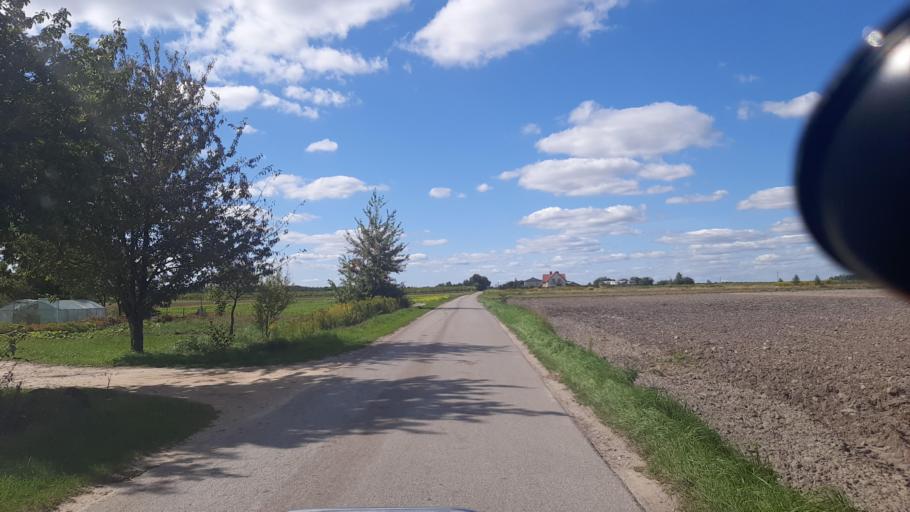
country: PL
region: Lublin Voivodeship
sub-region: Powiat lubartowski
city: Kamionka
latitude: 51.4047
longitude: 22.4085
